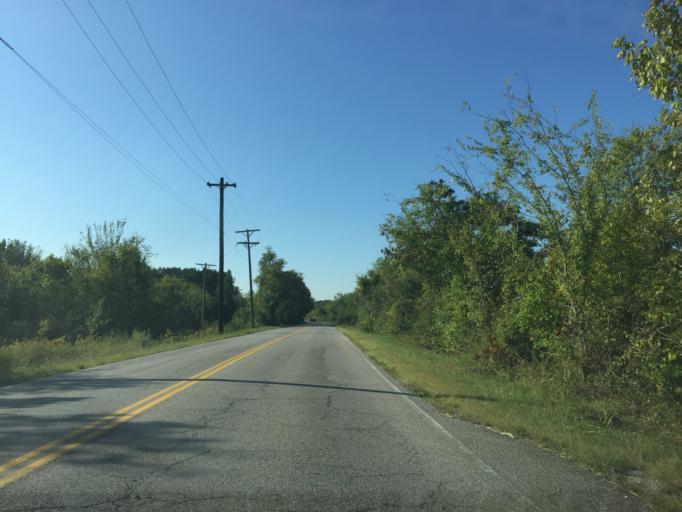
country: US
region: Tennessee
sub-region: Hamilton County
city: Harrison
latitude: 35.0947
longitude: -85.1603
